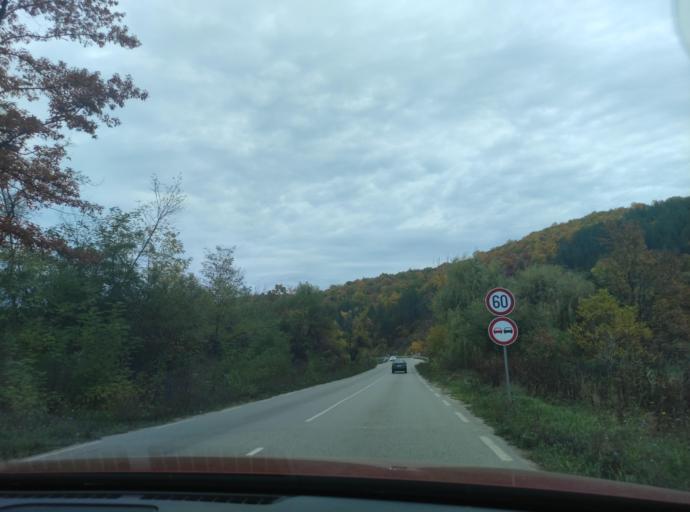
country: BG
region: Montana
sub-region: Obshtina Berkovitsa
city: Berkovitsa
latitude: 43.2606
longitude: 23.1769
